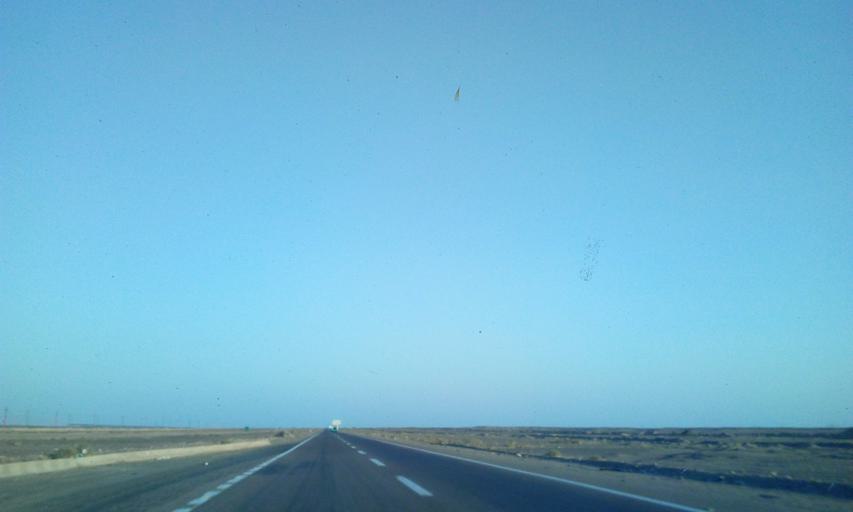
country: EG
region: South Sinai
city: Tor
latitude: 28.0595
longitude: 33.2715
